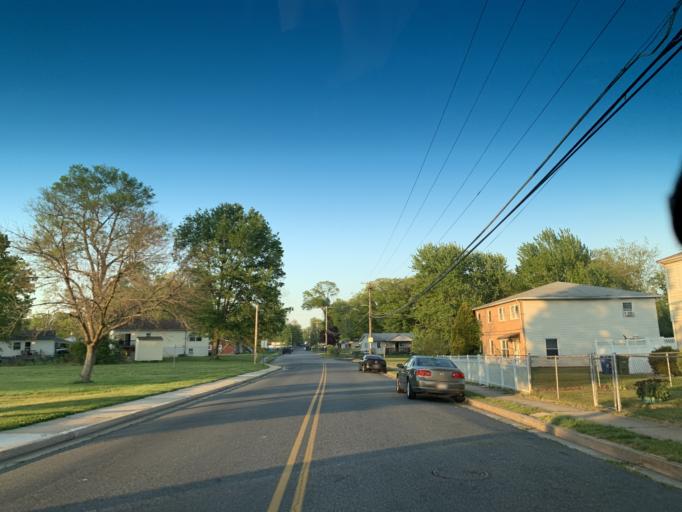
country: US
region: Maryland
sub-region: Harford County
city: Aberdeen
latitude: 39.5033
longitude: -76.1784
